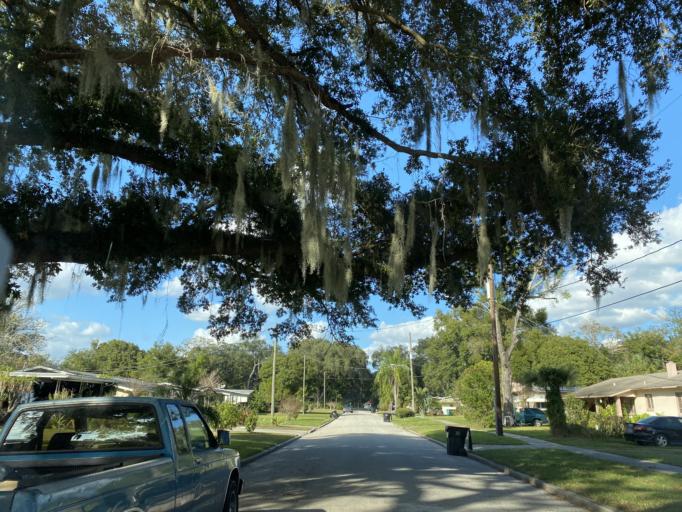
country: US
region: Florida
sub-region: Orange County
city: Orlando
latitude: 28.5499
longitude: -81.4036
